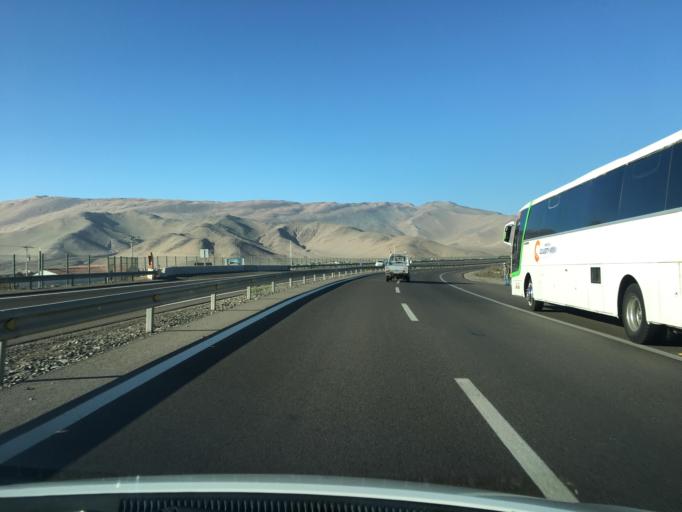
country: CL
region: Atacama
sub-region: Provincia de Copiapo
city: Copiapo
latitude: -27.2997
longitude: -70.4884
